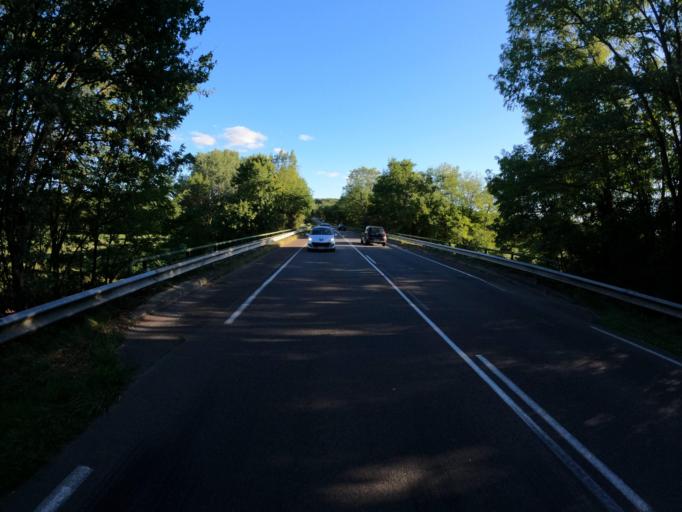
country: FR
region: Bourgogne
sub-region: Departement de Saone-et-Loire
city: Torcy
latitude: 46.7500
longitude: 4.4412
